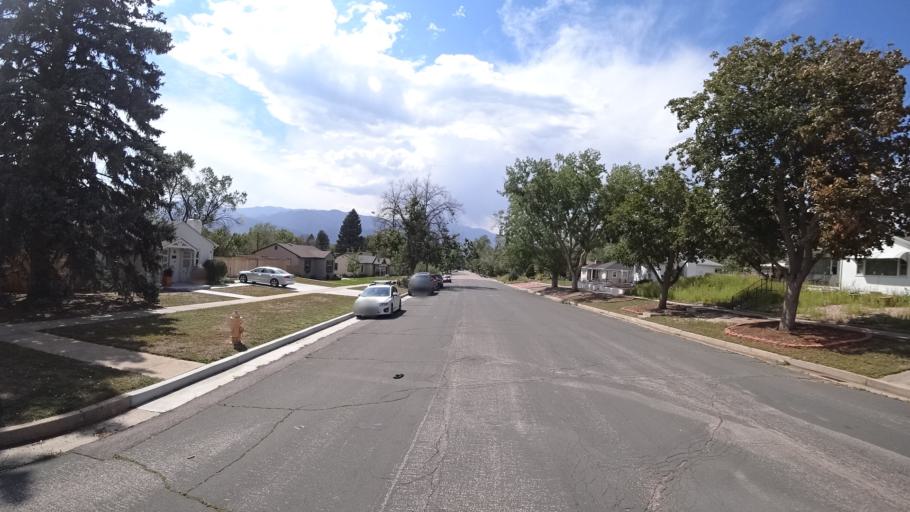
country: US
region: Colorado
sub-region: El Paso County
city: Colorado Springs
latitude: 38.8472
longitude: -104.8002
